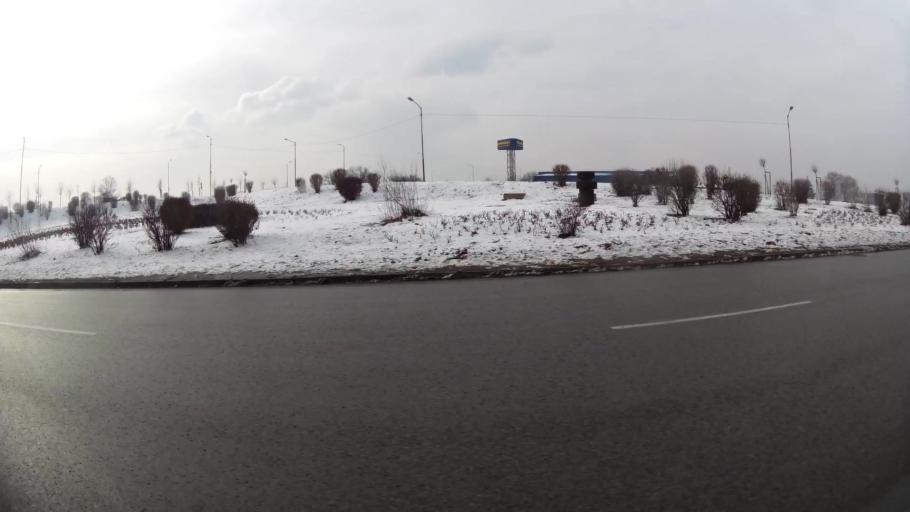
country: BG
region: Sofia-Capital
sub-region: Stolichna Obshtina
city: Sofia
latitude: 42.7068
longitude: 23.4021
